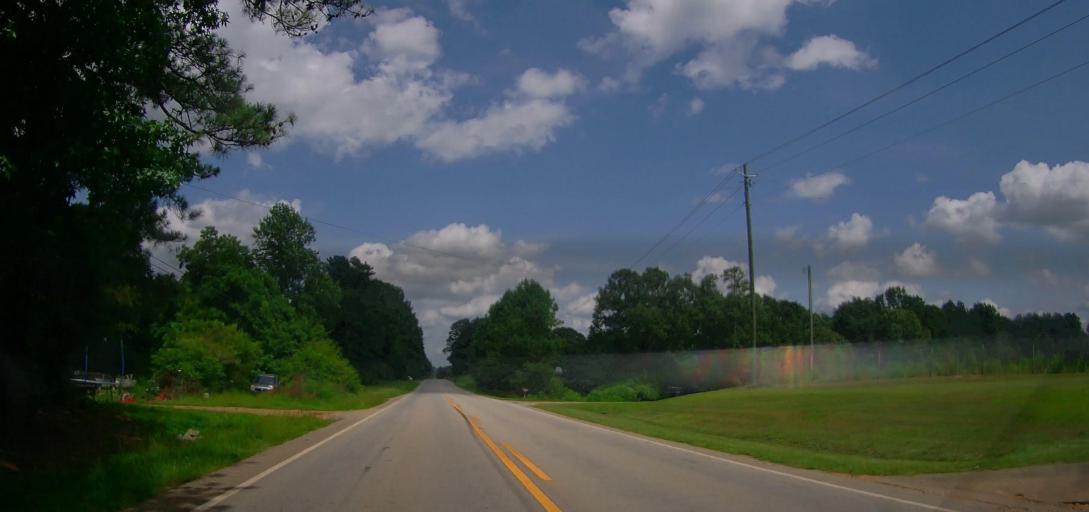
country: US
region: Georgia
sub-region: Carroll County
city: Bowdon
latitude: 33.5393
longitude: -85.3845
